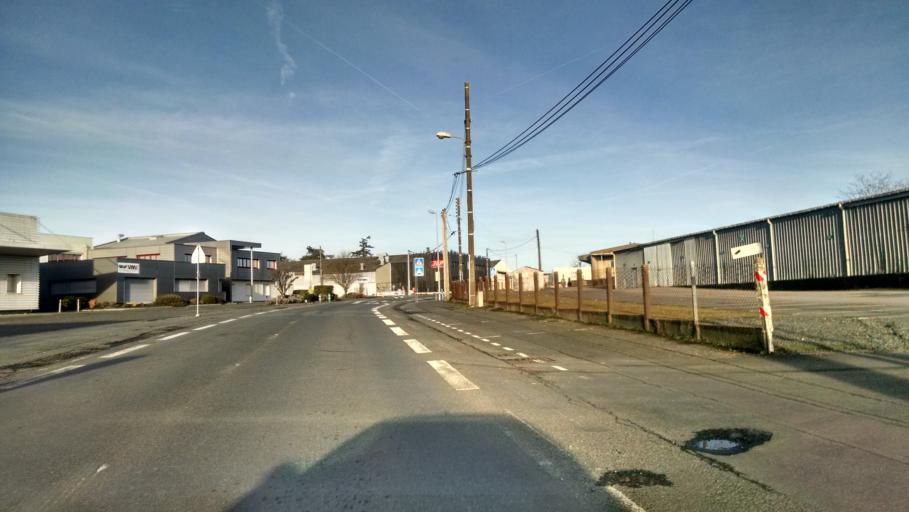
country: FR
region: Pays de la Loire
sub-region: Departement de la Vendee
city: Montaigu
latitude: 46.9827
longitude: -1.3218
